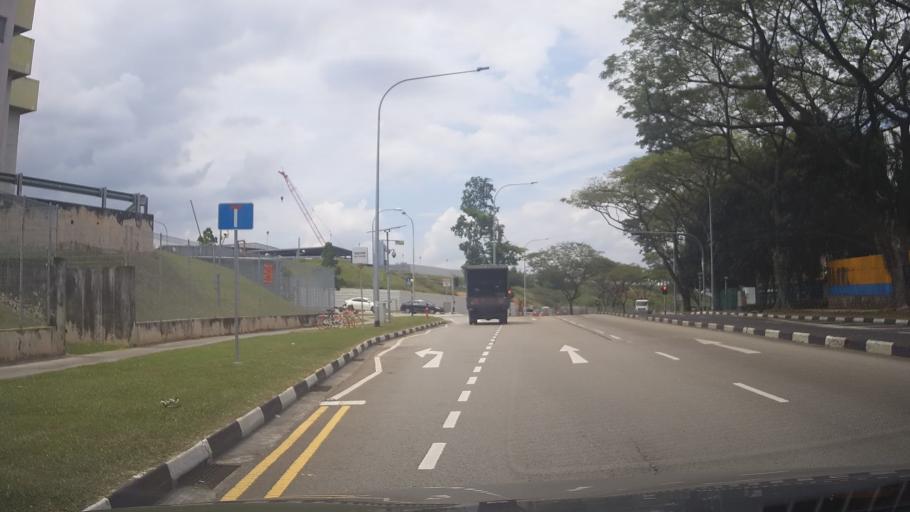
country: MY
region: Johor
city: Johor Bahru
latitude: 1.4570
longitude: 103.7954
